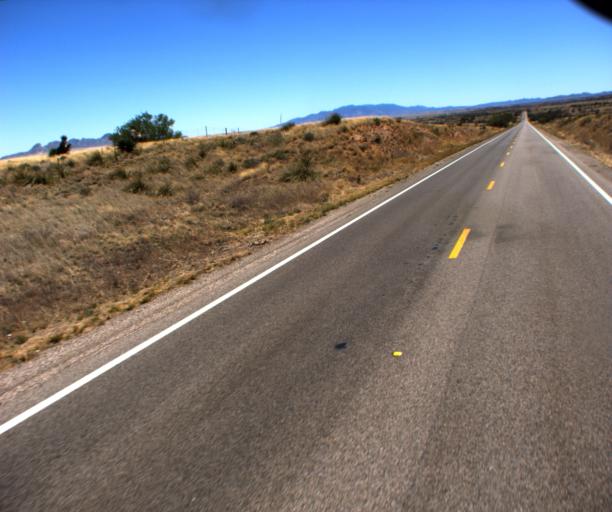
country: US
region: Arizona
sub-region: Pima County
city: Corona de Tucson
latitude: 31.7619
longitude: -110.6785
